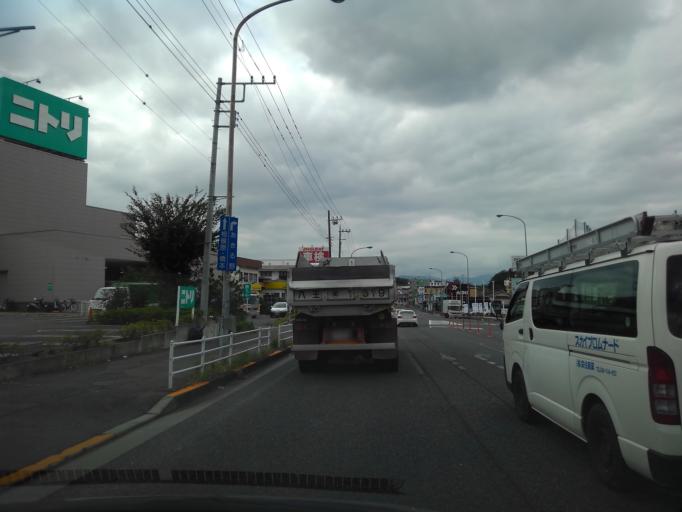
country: JP
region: Tokyo
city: Hachioji
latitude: 35.6787
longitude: 139.3372
